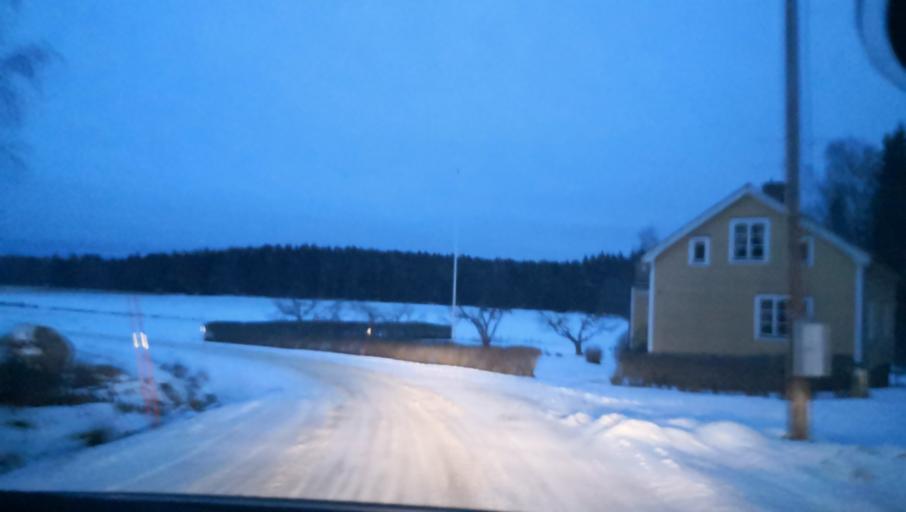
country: SE
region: Dalarna
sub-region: Avesta Kommun
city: Horndal
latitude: 60.2412
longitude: 16.6788
